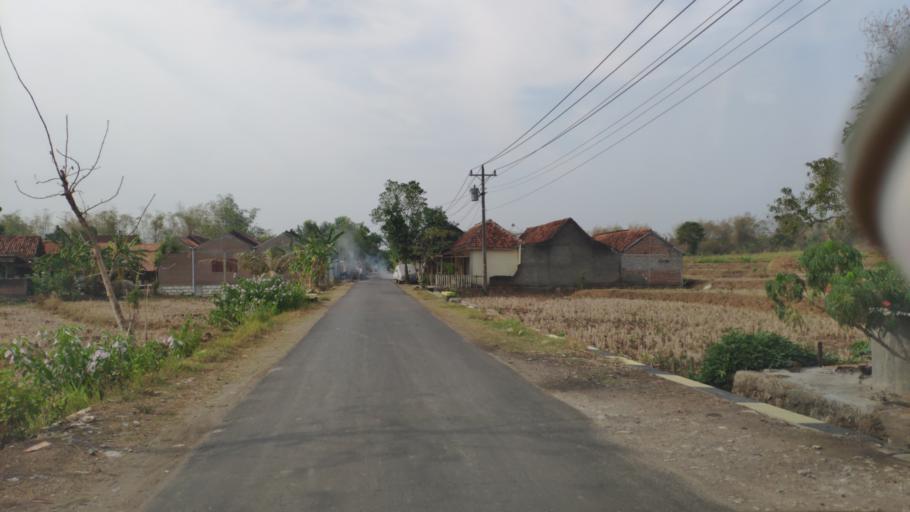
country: ID
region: Central Java
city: Tawangsari
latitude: -6.9768
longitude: 111.3426
